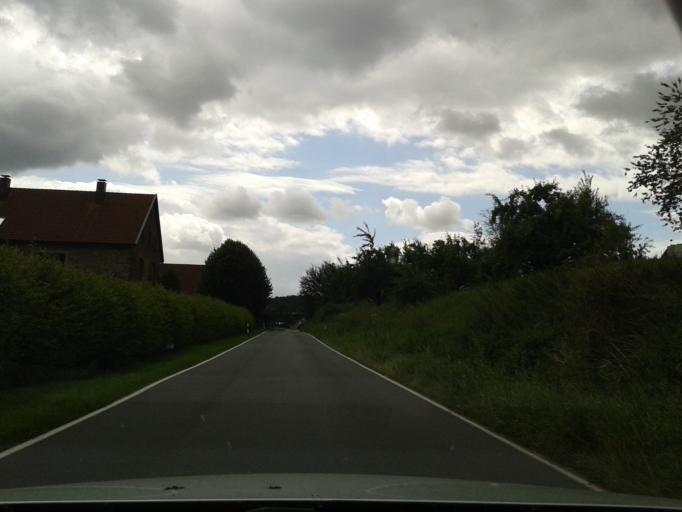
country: DE
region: North Rhine-Westphalia
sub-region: Regierungsbezirk Detmold
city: Barntrup
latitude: 52.0128
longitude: 9.0590
